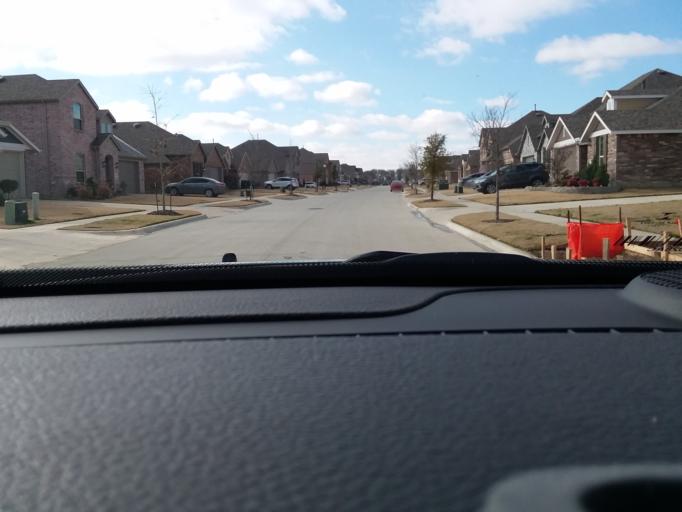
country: US
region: Texas
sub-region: Denton County
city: Little Elm
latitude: 33.2408
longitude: -96.8970
